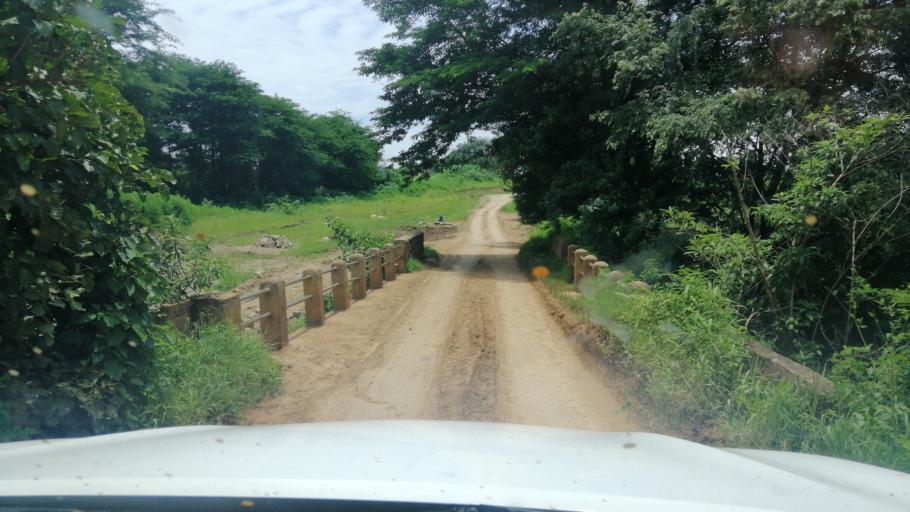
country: ET
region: Oromiya
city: Mendi
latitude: 10.1693
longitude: 35.0908
